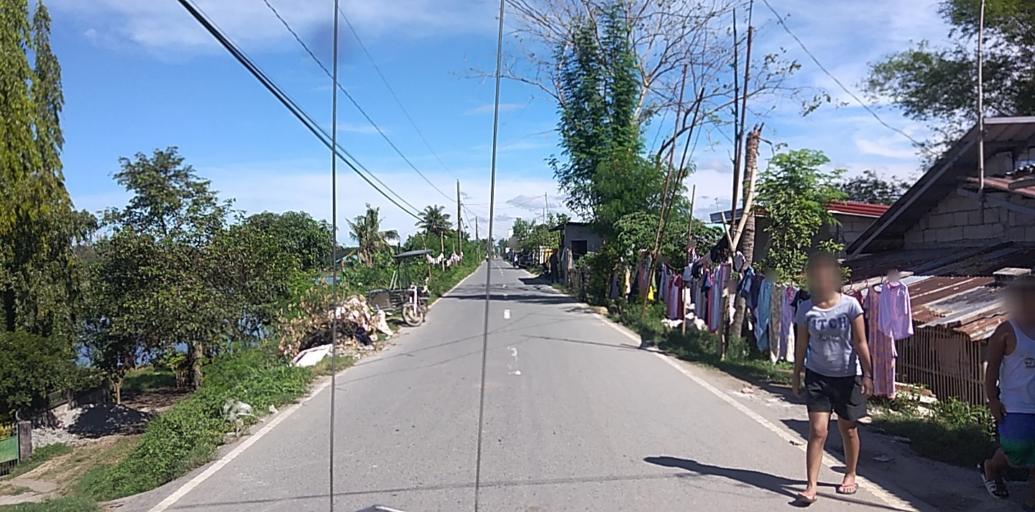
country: PH
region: Central Luzon
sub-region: Province of Pampanga
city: Candaba
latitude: 15.0949
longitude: 120.8128
